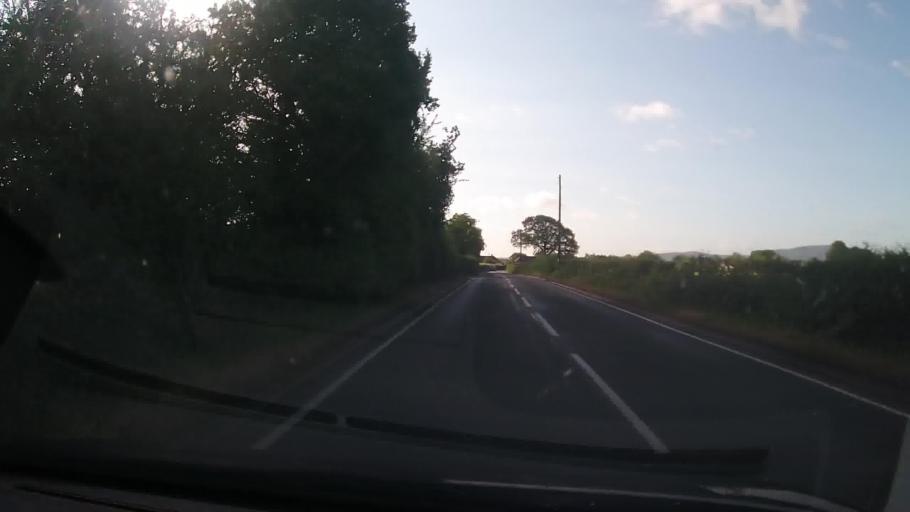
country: GB
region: England
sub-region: Shropshire
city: Withington
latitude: 52.7412
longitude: -2.5753
